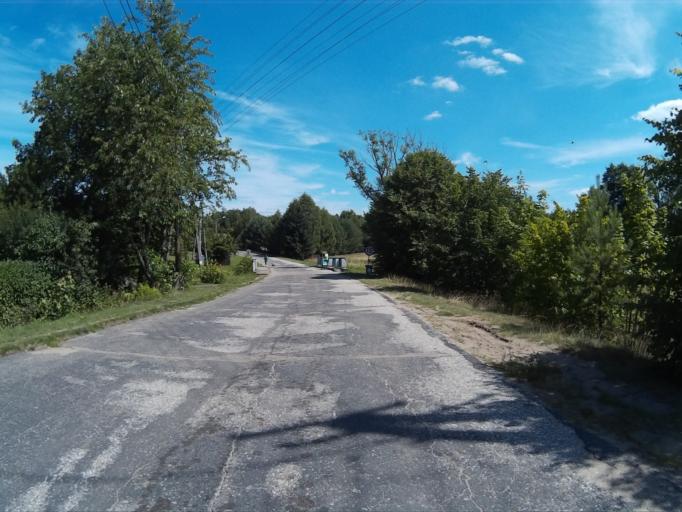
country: PL
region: Kujawsko-Pomorskie
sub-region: Powiat tucholski
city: Cekcyn
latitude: 53.6791
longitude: 17.9752
